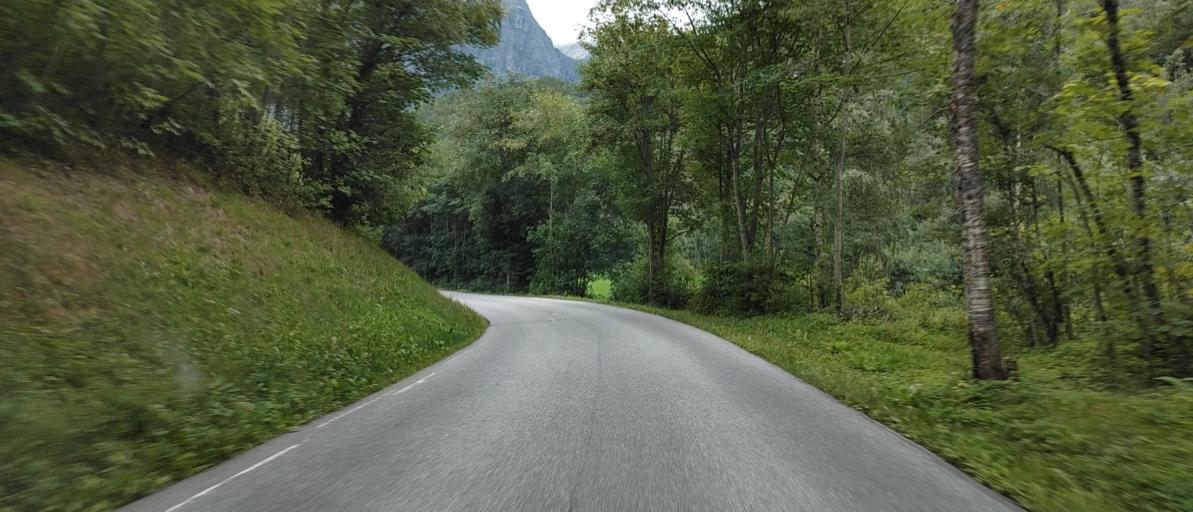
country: NO
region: More og Romsdal
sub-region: Rauma
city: Andalsnes
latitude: 62.5266
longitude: 7.7156
